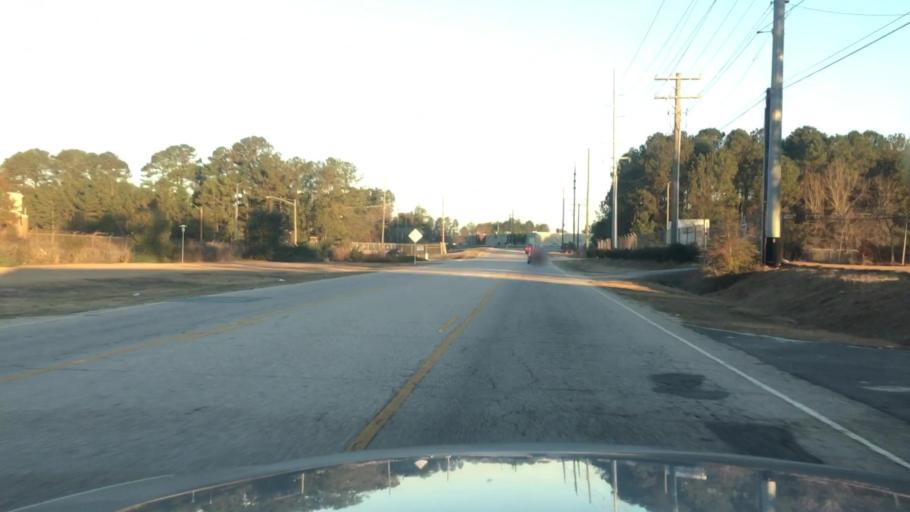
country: US
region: North Carolina
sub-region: Cumberland County
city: Hope Mills
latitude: 34.9983
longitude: -78.9035
